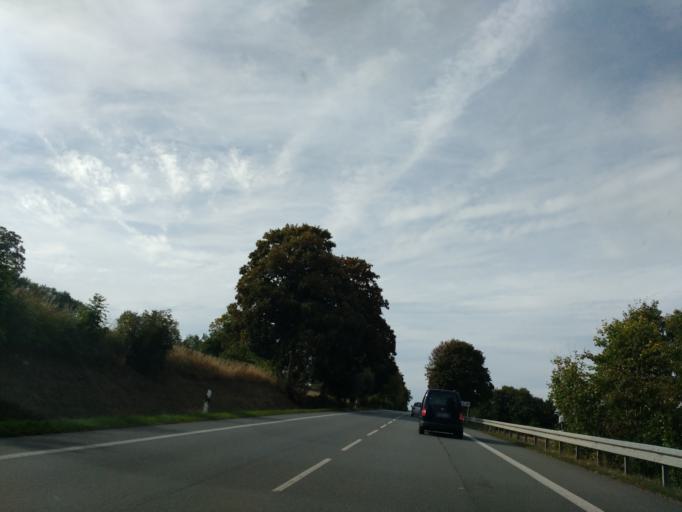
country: DE
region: North Rhine-Westphalia
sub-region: Regierungsbezirk Detmold
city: Nieheim
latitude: 51.8032
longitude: 9.1310
